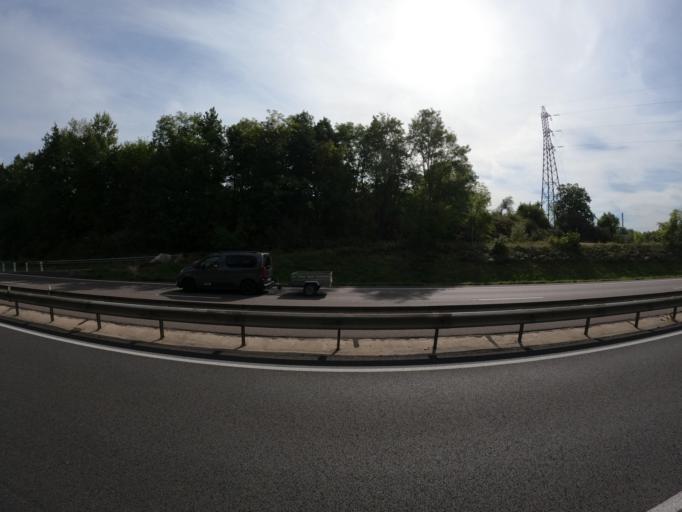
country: FR
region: Bourgogne
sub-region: Departement de Saone-et-Loire
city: Montceau-les-Mines
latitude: 46.6820
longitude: 4.3480
